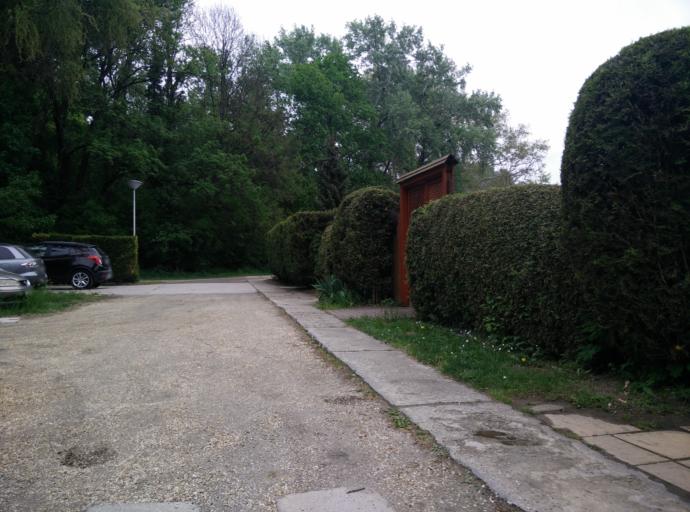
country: HU
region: Pest
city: Fot
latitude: 47.6053
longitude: 19.1859
